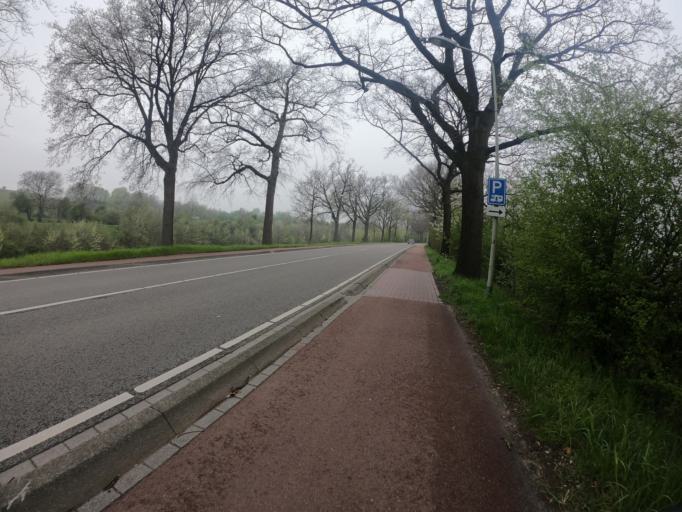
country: NL
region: Limburg
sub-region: Gemeente Maastricht
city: Maastricht
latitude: 50.8743
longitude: 5.6808
